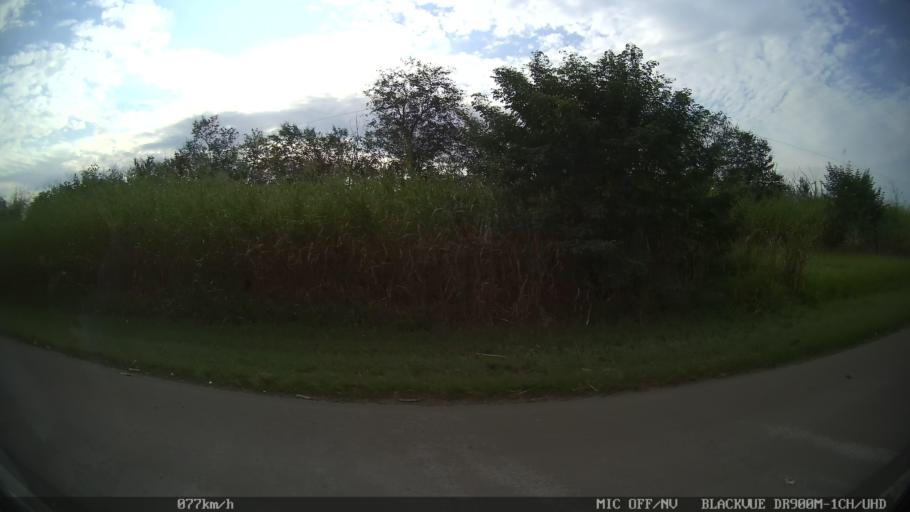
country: BR
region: Sao Paulo
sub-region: Cosmopolis
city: Cosmopolis
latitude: -22.6154
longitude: -47.2429
